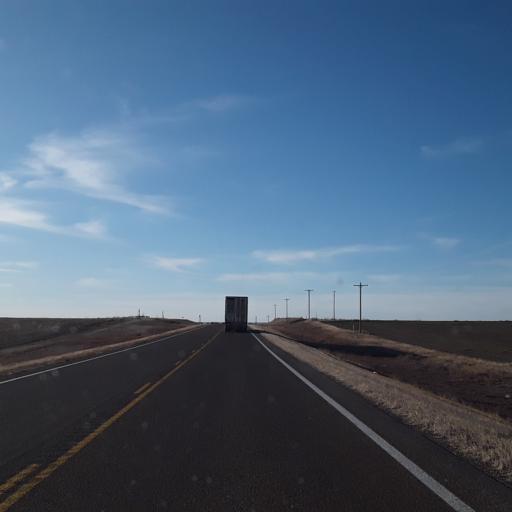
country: US
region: Kansas
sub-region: Cheyenne County
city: Saint Francis
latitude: 39.7566
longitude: -101.6897
